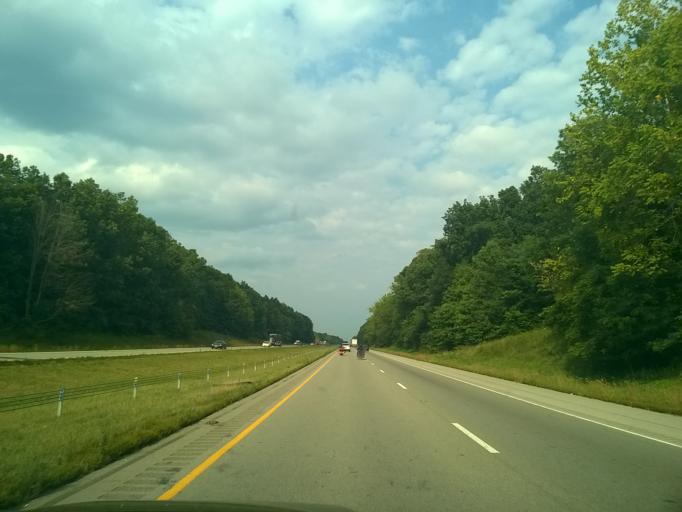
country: US
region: Indiana
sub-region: Clay County
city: Brazil
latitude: 39.4924
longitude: -86.9873
